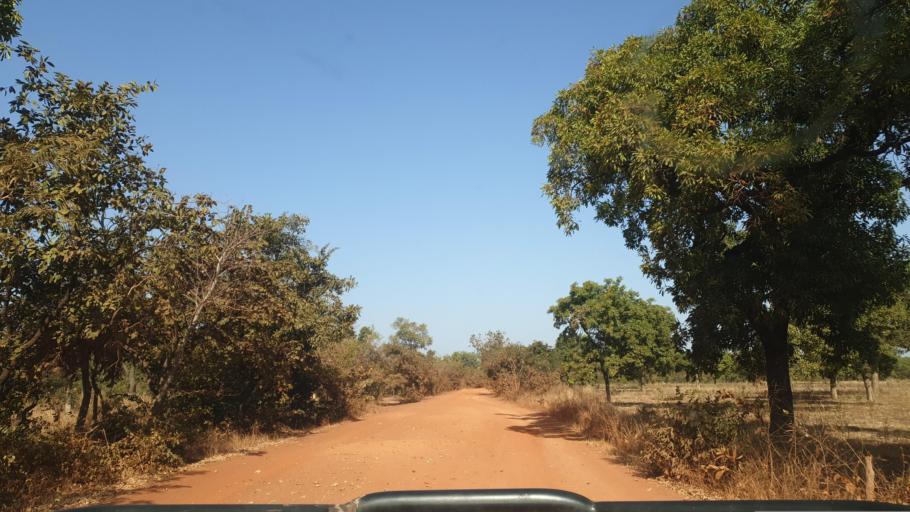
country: ML
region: Sikasso
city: Bougouni
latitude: 11.7755
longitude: -6.9054
